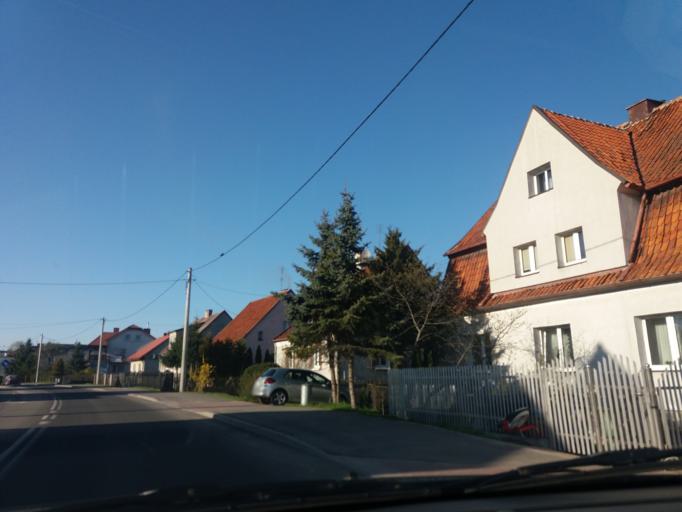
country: PL
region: Warmian-Masurian Voivodeship
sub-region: Powiat nidzicki
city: Nidzica
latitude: 53.3680
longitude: 20.4298
